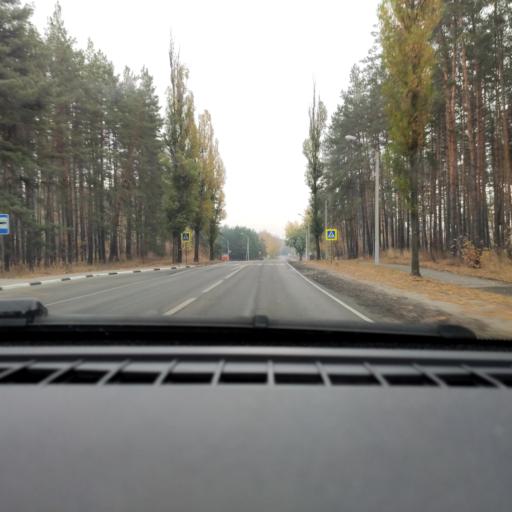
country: RU
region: Voronezj
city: Somovo
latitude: 51.6990
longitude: 39.3207
